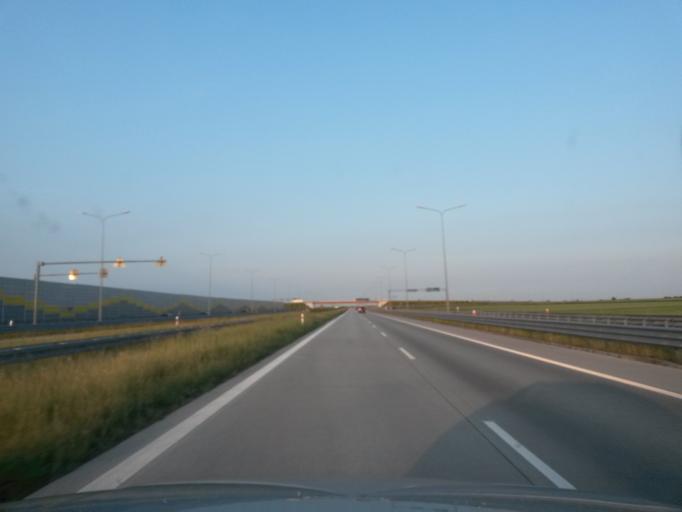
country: PL
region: Lodz Voivodeship
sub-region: Powiat wieruszowski
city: Walichnowy
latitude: 51.3168
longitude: 18.3769
